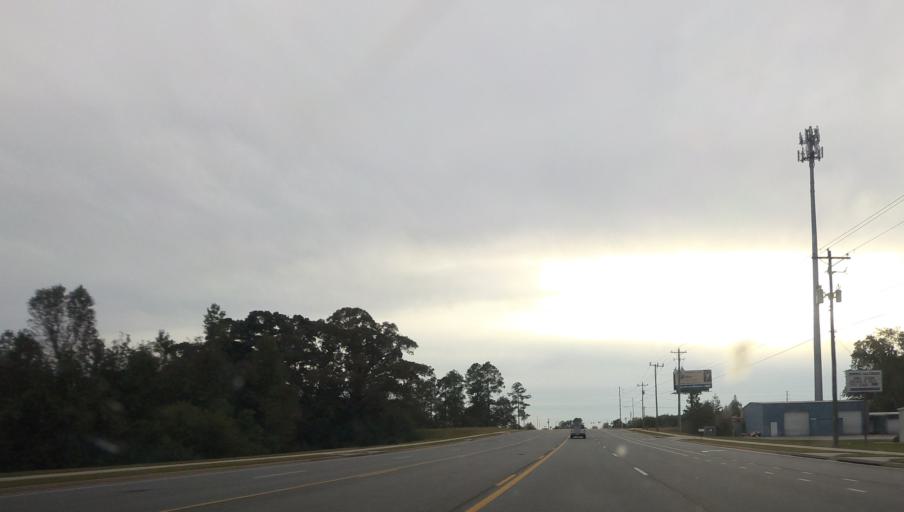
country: US
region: Georgia
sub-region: Houston County
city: Perry
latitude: 32.4780
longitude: -83.7012
